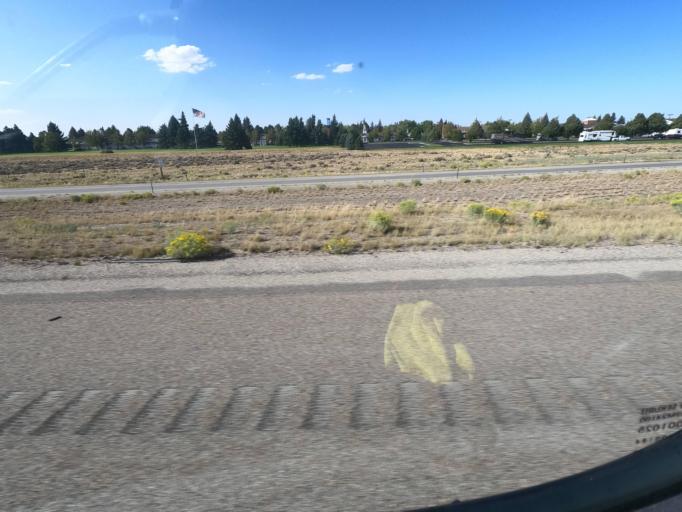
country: US
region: Wyoming
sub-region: Sweetwater County
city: Green River
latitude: 41.5425
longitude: -109.8599
